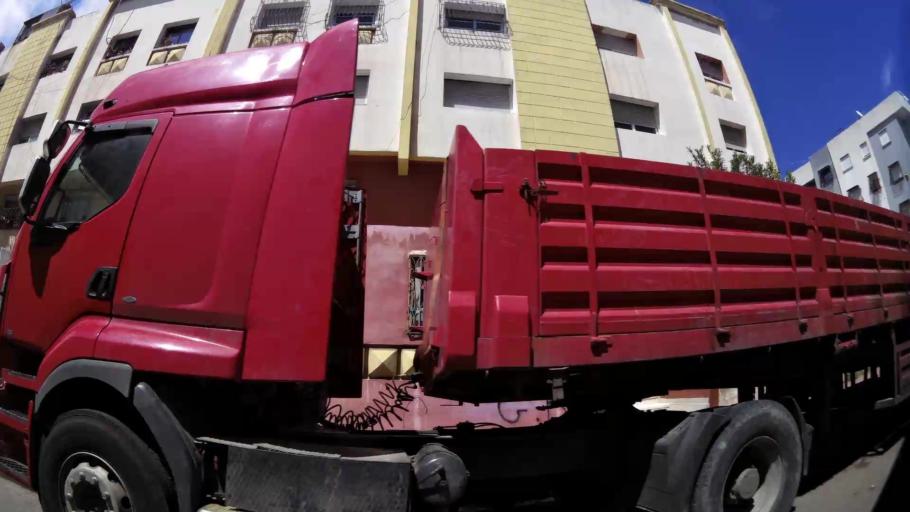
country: MA
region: Grand Casablanca
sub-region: Mediouna
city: Tit Mellil
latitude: 33.5992
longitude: -7.4821
